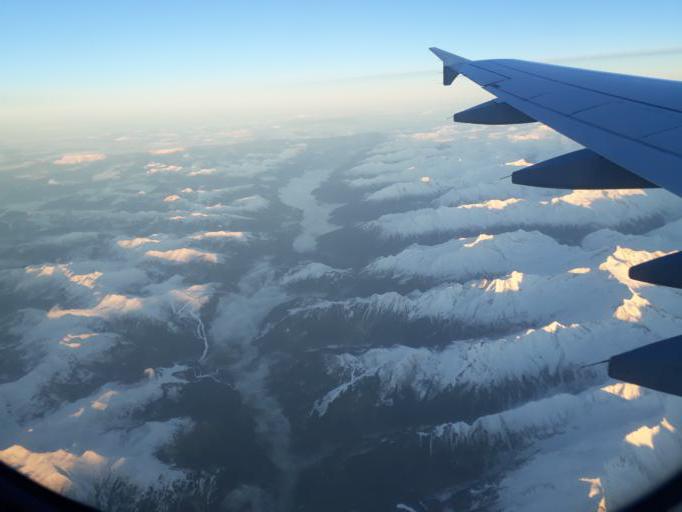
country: AT
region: Tyrol
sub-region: Politischer Bezirk Schwaz
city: Ramsau im Zillertal
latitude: 47.1857
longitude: 11.8907
